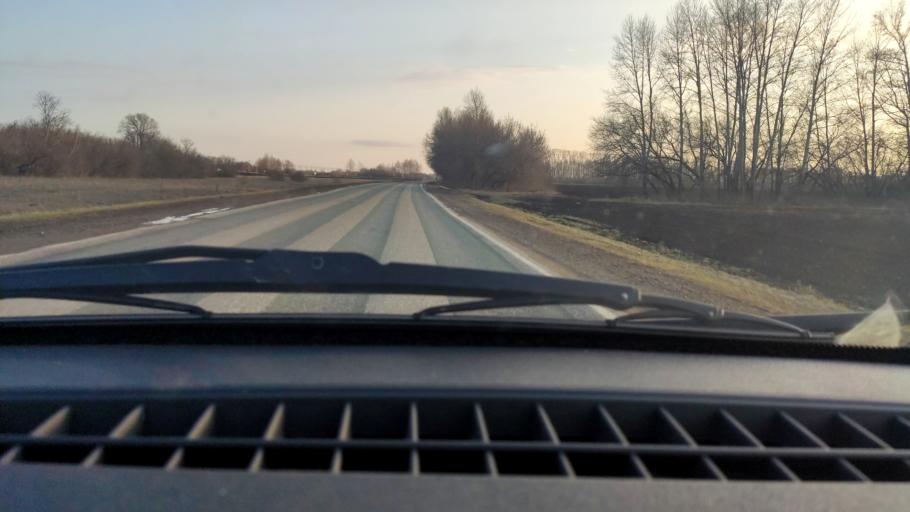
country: RU
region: Bashkortostan
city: Chishmy
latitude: 54.4548
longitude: 55.2511
